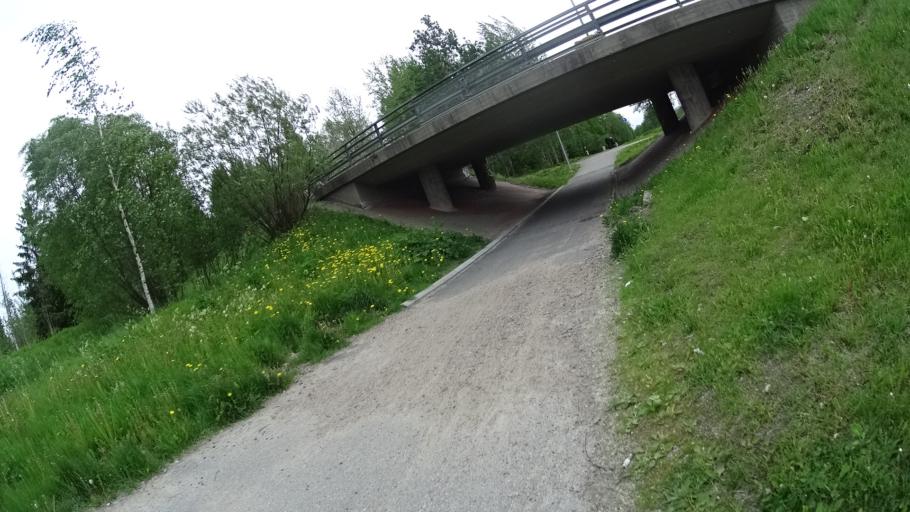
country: FI
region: Uusimaa
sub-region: Helsinki
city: Vantaa
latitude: 60.2858
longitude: 25.0597
